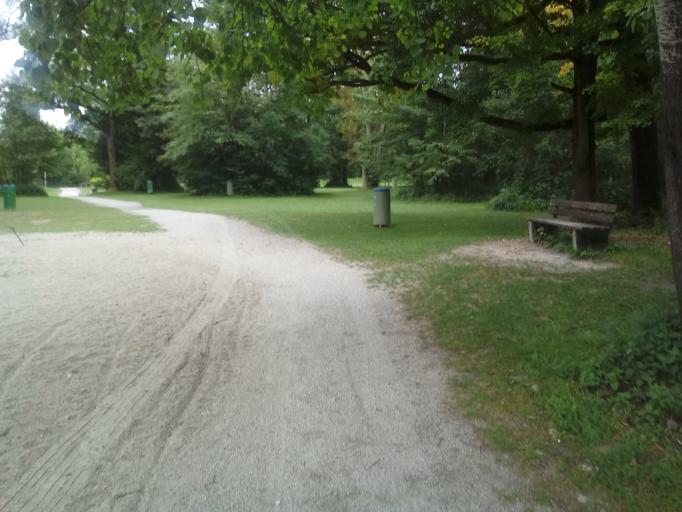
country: DE
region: Bavaria
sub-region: Upper Bavaria
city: Unterfoehring
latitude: 48.2026
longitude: 11.6442
